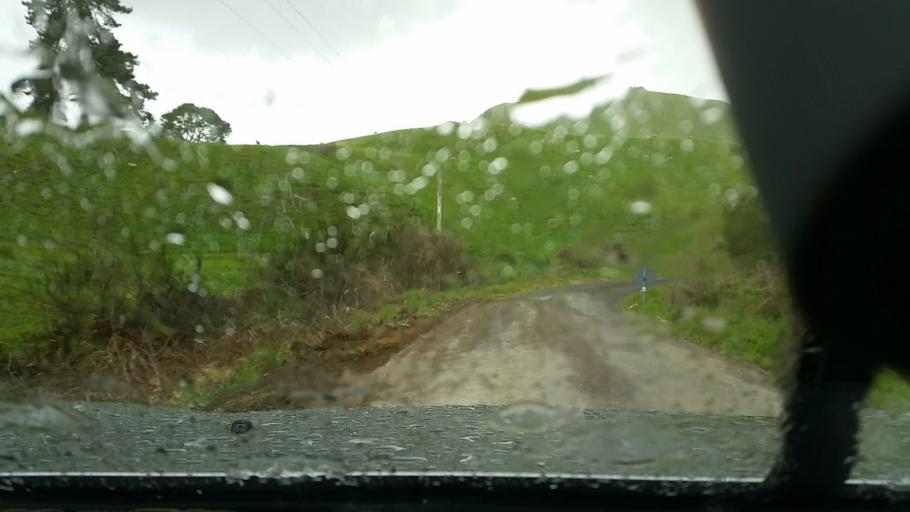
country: NZ
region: Waikato
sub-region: Taupo District
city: Taupo
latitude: -38.4727
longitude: 176.2246
